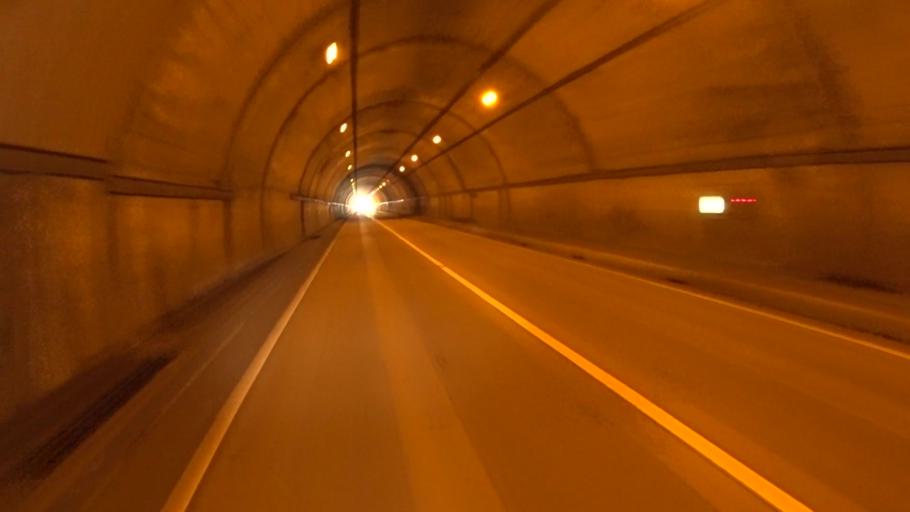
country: JP
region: Kyoto
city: Fukuchiyama
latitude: 35.4112
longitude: 135.0854
